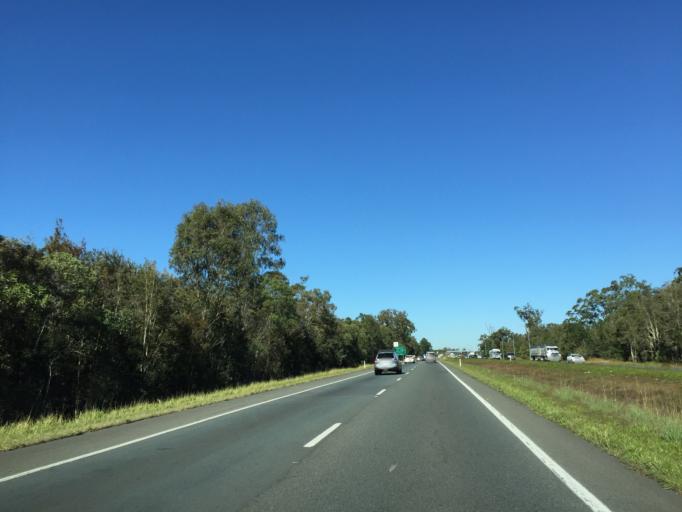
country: AU
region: Queensland
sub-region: Moreton Bay
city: Caboolture
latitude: -27.0608
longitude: 152.9774
